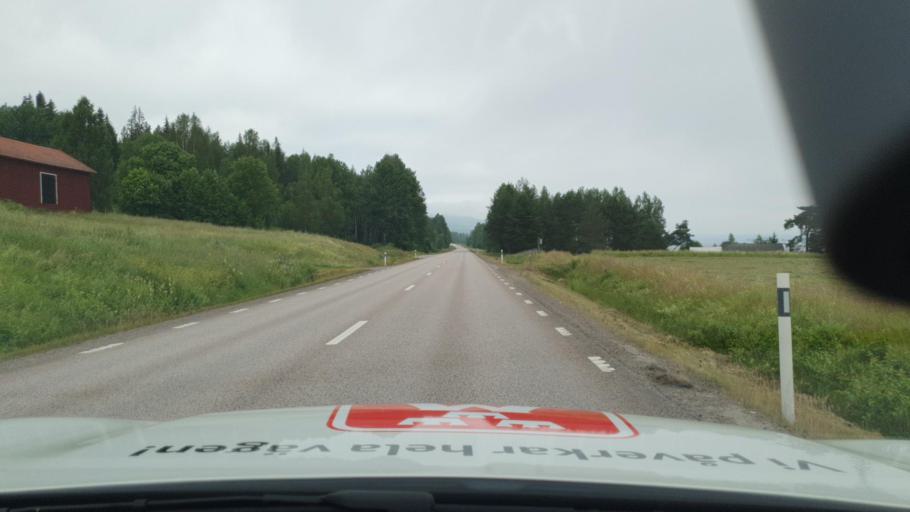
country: SE
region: Vaermland
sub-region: Sunne Kommun
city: Sunne
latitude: 59.9343
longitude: 13.1241
